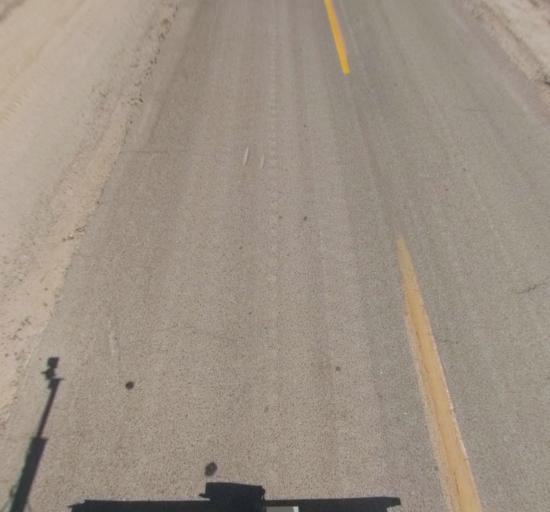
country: US
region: California
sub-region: Fresno County
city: Mendota
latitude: 36.8172
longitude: -120.2591
